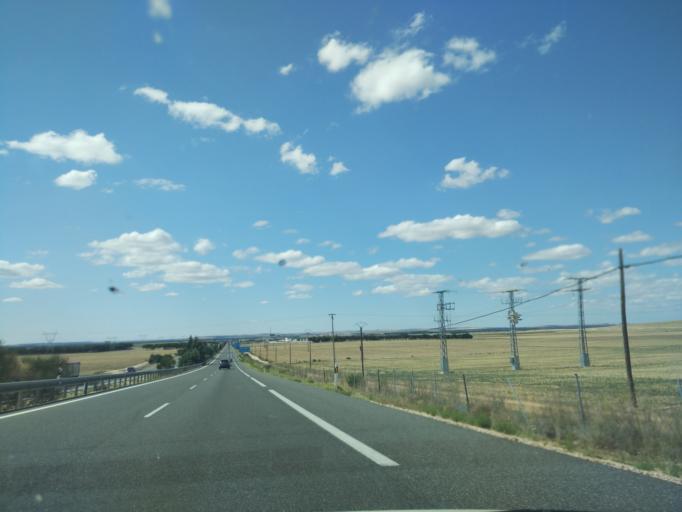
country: ES
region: Castille and Leon
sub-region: Provincia de Valladolid
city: San Vicente del Palacio
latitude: 41.2097
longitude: -4.8318
